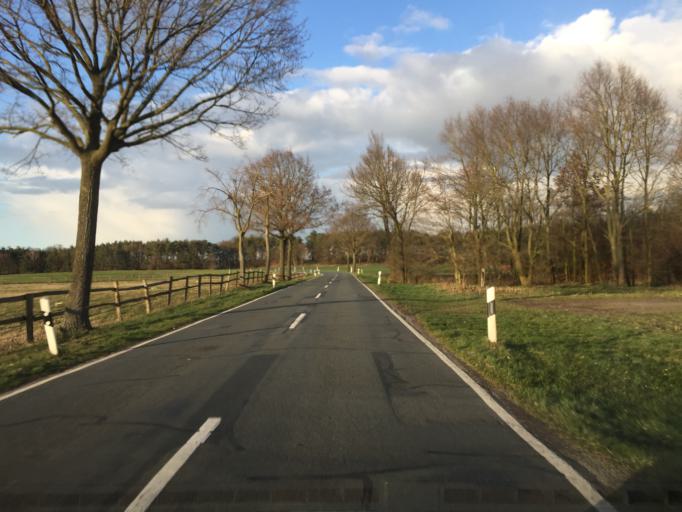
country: DE
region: Lower Saxony
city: Steyerberg
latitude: 52.5832
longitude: 8.9781
